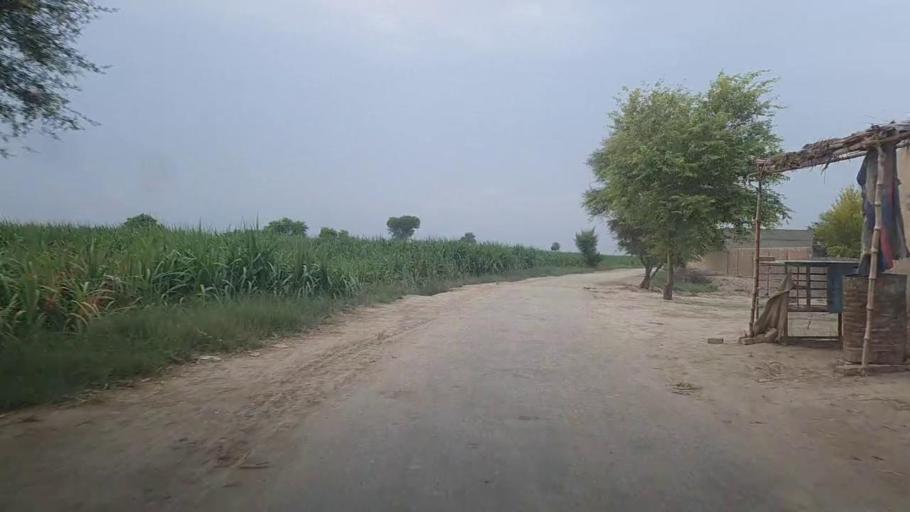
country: PK
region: Sindh
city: Kashmor
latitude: 28.3729
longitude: 69.7835
